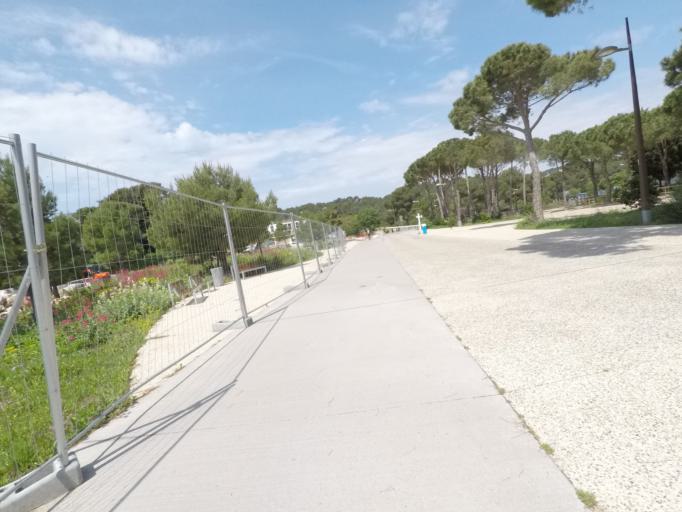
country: FR
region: Provence-Alpes-Cote d'Azur
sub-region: Departement des Bouches-du-Rhone
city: Marseille 09
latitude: 43.2312
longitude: 5.4388
